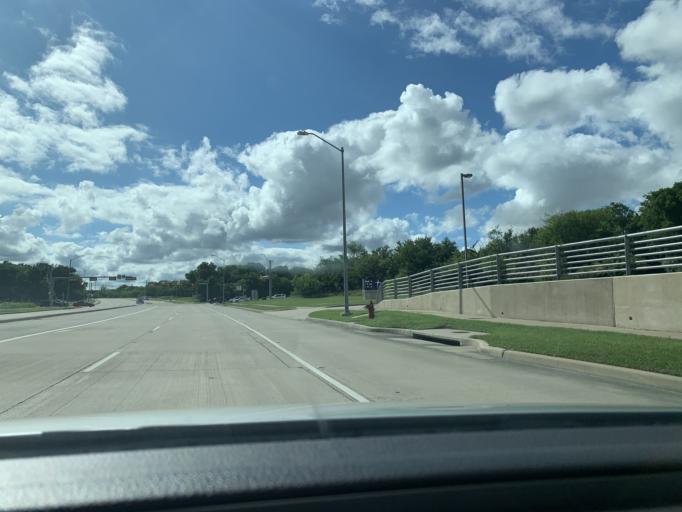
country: US
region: Texas
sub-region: Dallas County
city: Grand Prairie
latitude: 32.6680
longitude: -97.0227
